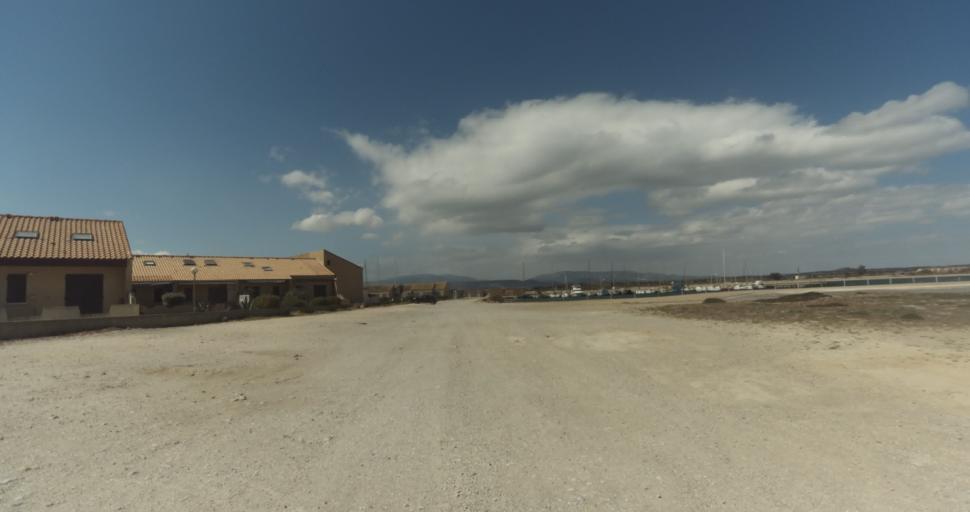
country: FR
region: Languedoc-Roussillon
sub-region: Departement de l'Aude
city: Leucate
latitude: 42.8695
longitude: 3.0479
